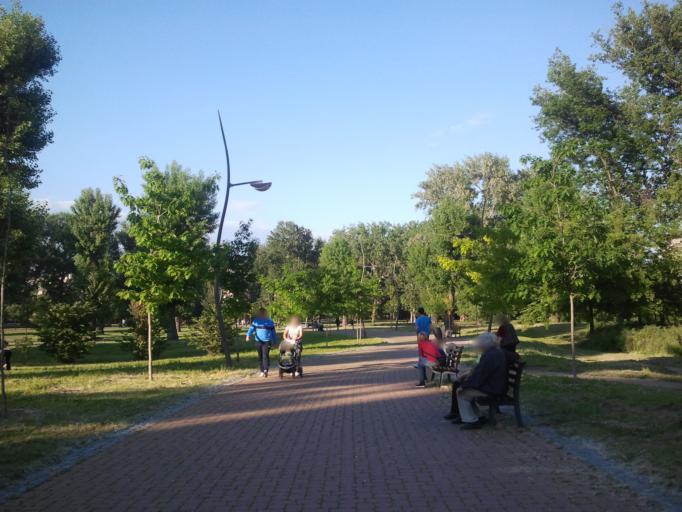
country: RS
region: Autonomna Pokrajina Vojvodina
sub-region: Juznobacki Okrug
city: Novi Sad
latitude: 45.2383
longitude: 19.8396
